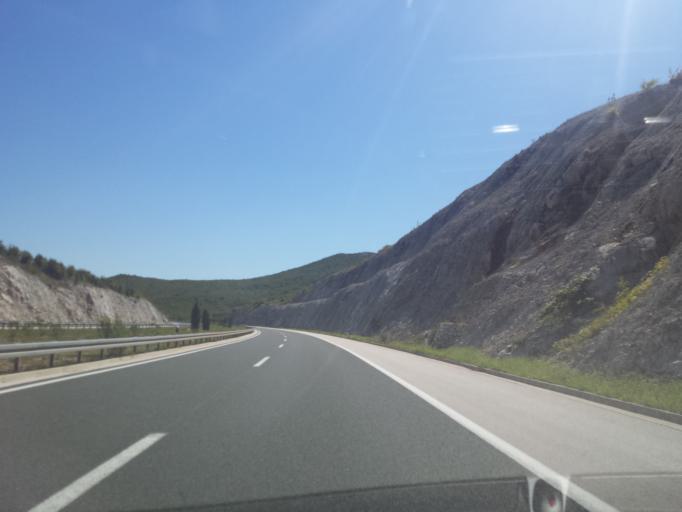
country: HR
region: Splitsko-Dalmatinska
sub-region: Grad Omis
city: Omis
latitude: 43.4803
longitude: 16.8073
